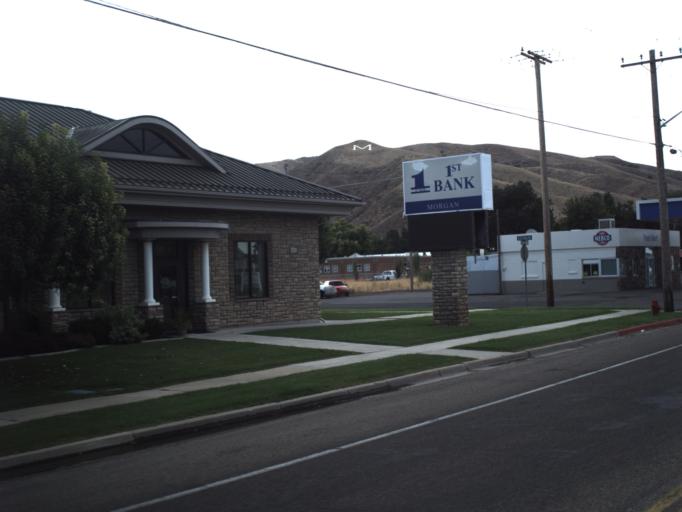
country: US
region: Utah
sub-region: Morgan County
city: Morgan
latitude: 41.0382
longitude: -111.6785
